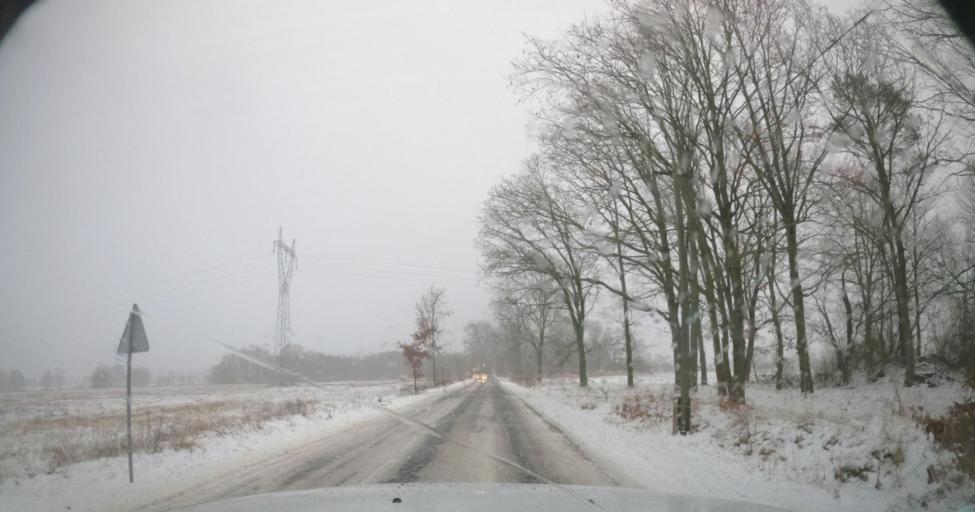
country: PL
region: West Pomeranian Voivodeship
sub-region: Powiat goleniowski
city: Przybiernow
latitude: 53.6894
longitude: 14.8491
